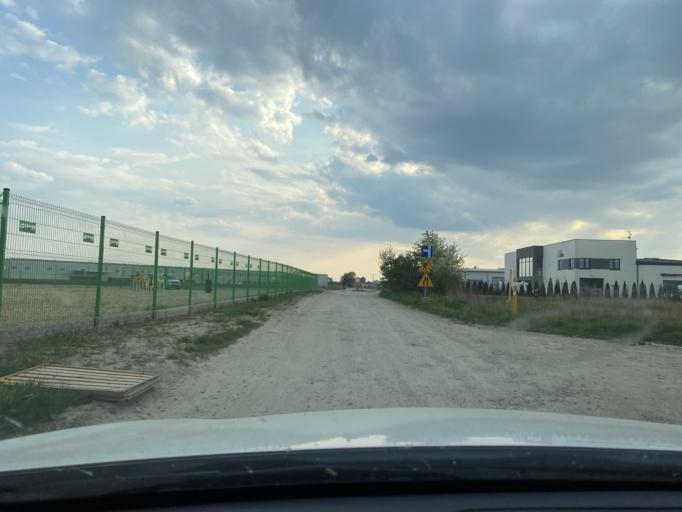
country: PL
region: Lower Silesian Voivodeship
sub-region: Powiat wroclawski
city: Mirkow
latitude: 51.1589
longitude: 17.1647
